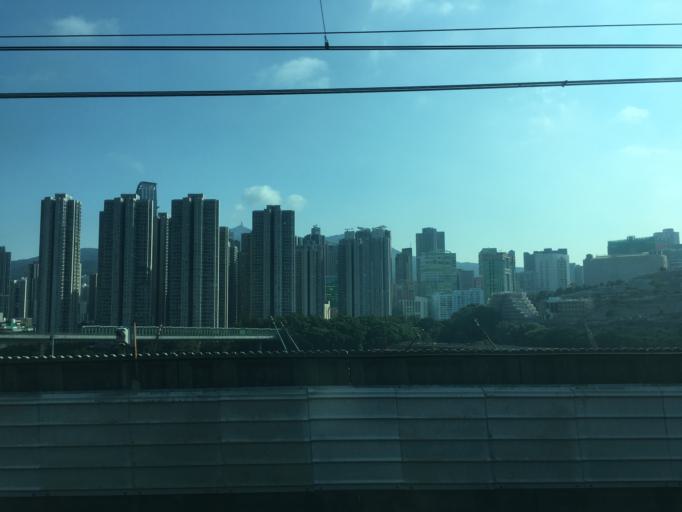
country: HK
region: Tsuen Wan
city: Tsuen Wan
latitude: 22.3569
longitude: 114.1124
